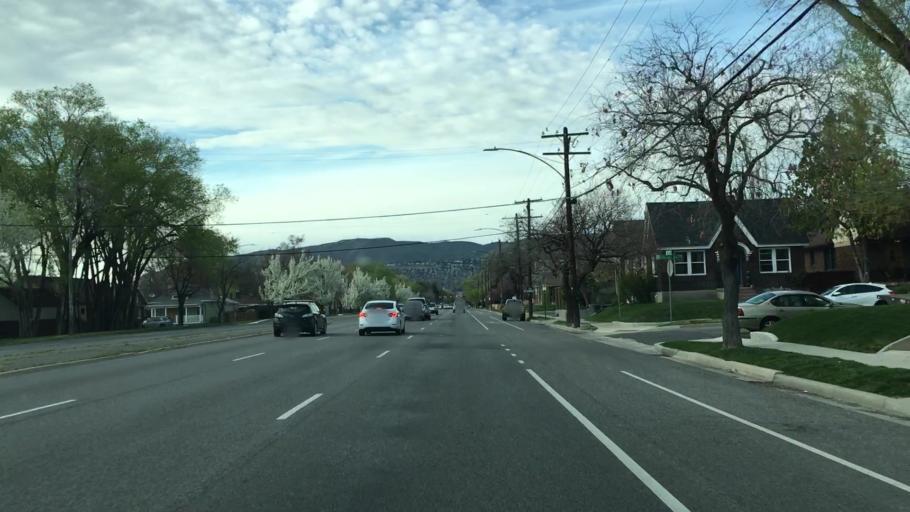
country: US
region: Utah
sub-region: Salt Lake County
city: South Salt Lake
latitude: 40.7370
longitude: -111.8711
